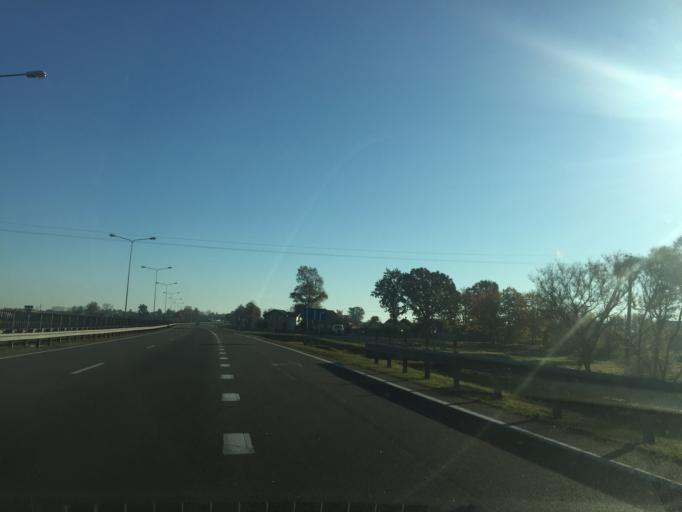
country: BY
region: Minsk
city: Smilavichy
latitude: 53.7584
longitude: 27.9719
